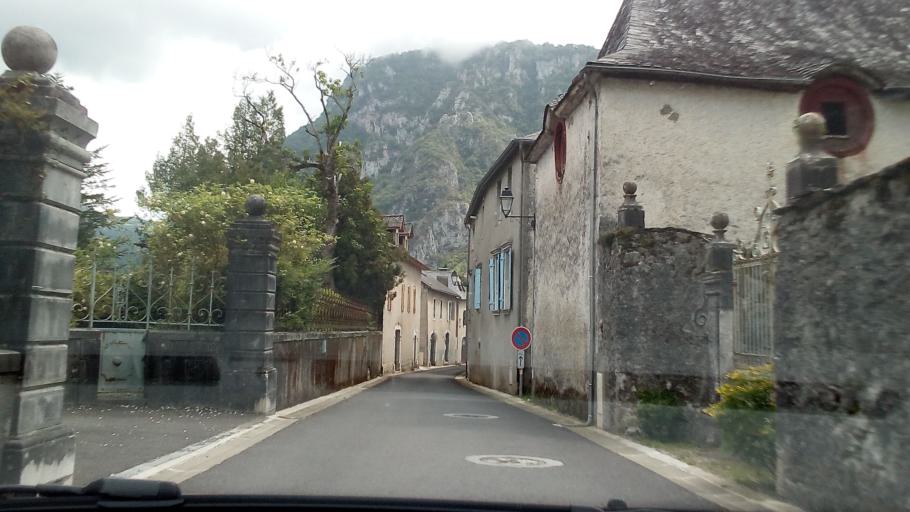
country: FR
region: Aquitaine
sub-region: Departement des Pyrenees-Atlantiques
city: Louvie-Juzon
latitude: 43.0556
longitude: -0.4334
